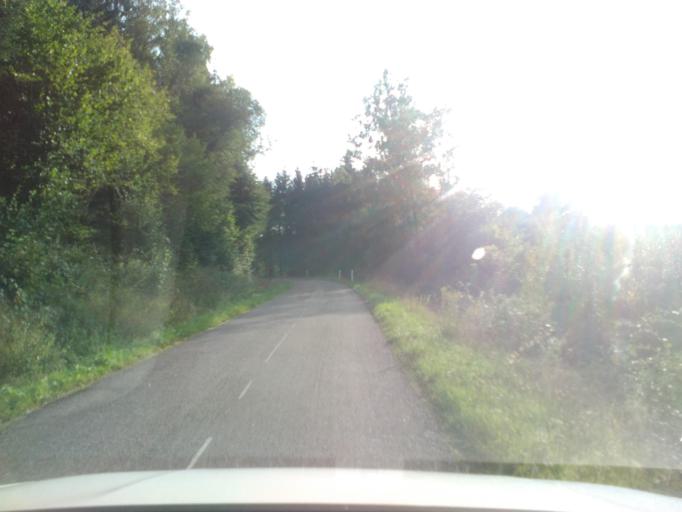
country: FR
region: Lorraine
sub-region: Departement des Vosges
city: Senones
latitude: 48.3831
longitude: 7.0443
